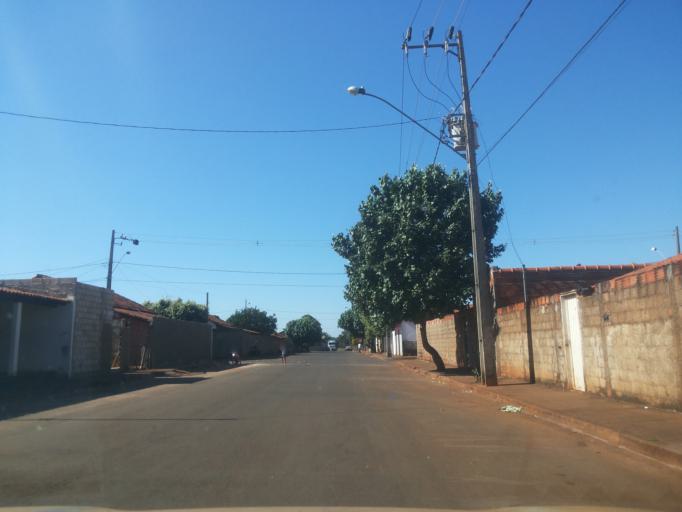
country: BR
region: Minas Gerais
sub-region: Centralina
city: Centralina
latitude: -18.7297
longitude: -49.1990
